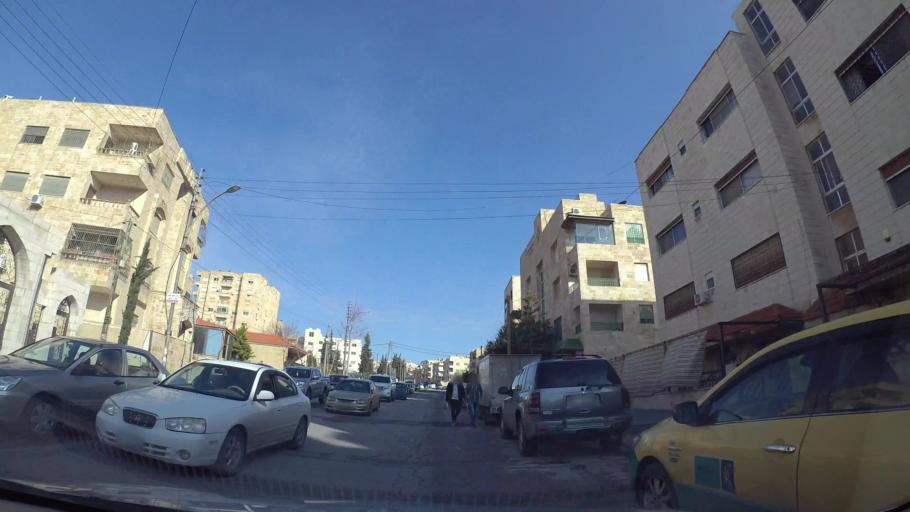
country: JO
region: Amman
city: Al Jubayhah
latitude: 31.9964
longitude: 35.8596
